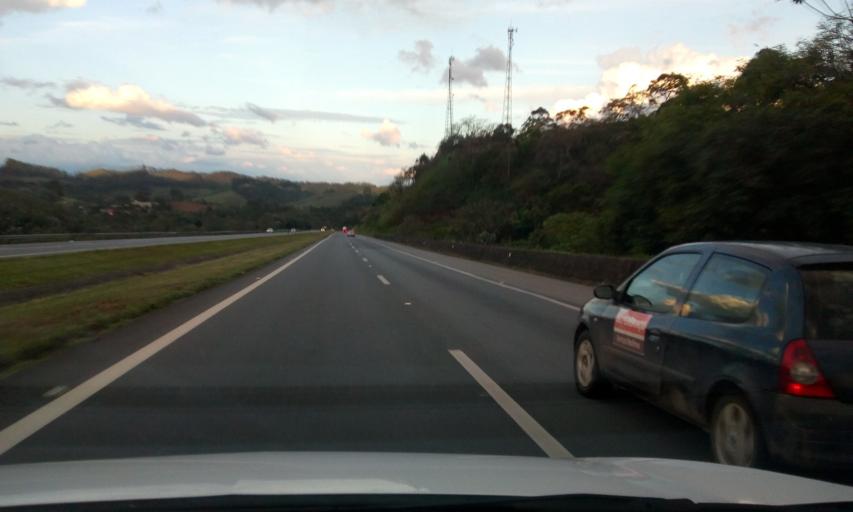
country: BR
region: Sao Paulo
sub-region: Santa Isabel
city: Santa Isabel
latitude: -23.1662
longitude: -46.2360
